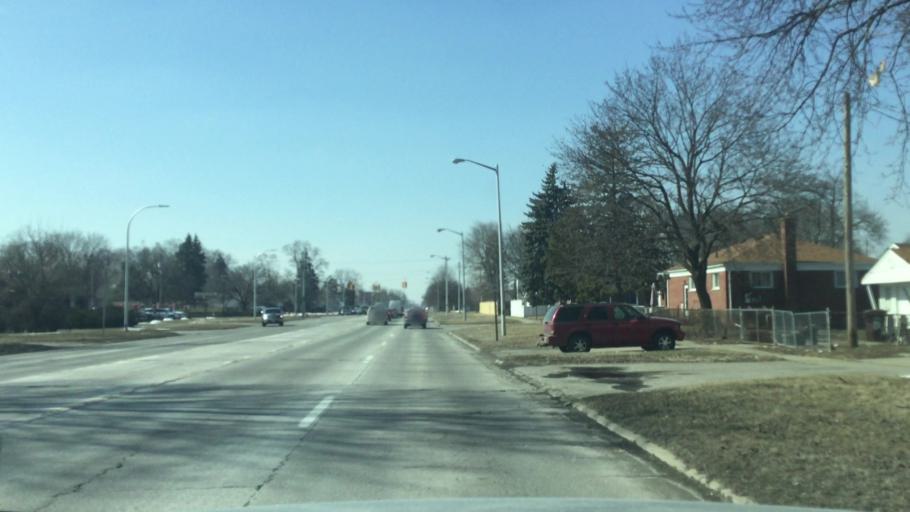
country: US
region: Michigan
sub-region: Wayne County
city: Garden City
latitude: 42.3115
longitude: -83.3190
